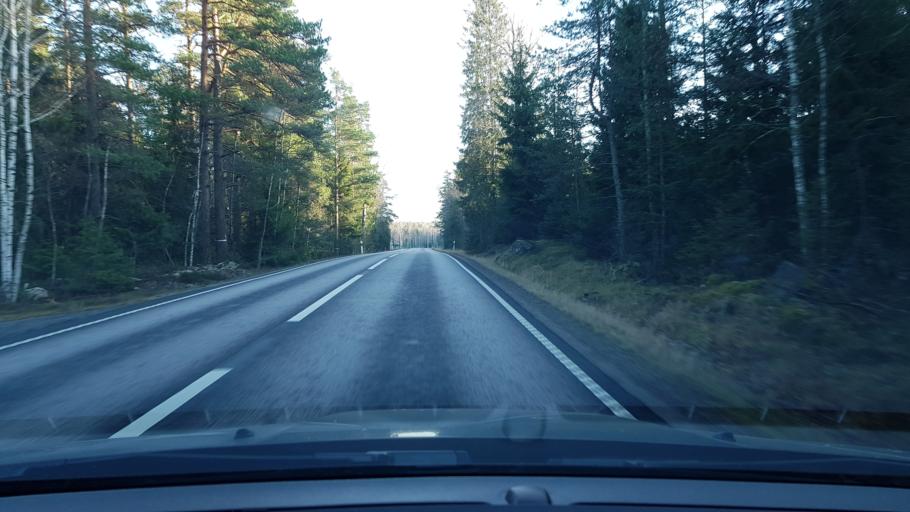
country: SE
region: Stockholm
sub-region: Norrtalje Kommun
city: Nykvarn
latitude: 59.7412
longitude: 18.2233
